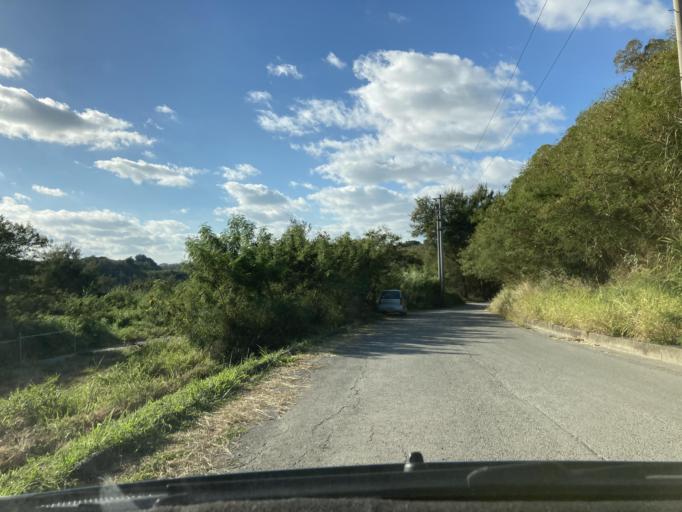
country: JP
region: Okinawa
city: Katsuren-haebaru
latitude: 26.3205
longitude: 127.9197
